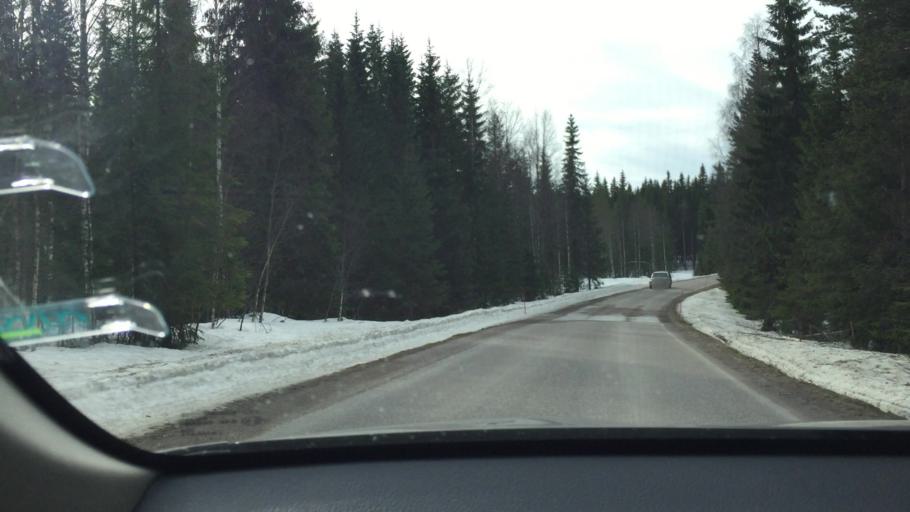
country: NO
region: Hedmark
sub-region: Trysil
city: Innbygda
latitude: 61.0671
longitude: 12.5481
